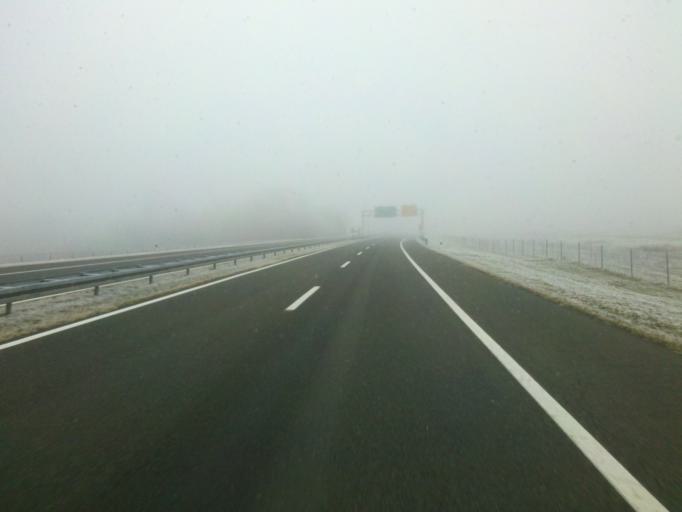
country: HR
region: Varazdinska
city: Jalzabet
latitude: 46.2906
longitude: 16.4891
